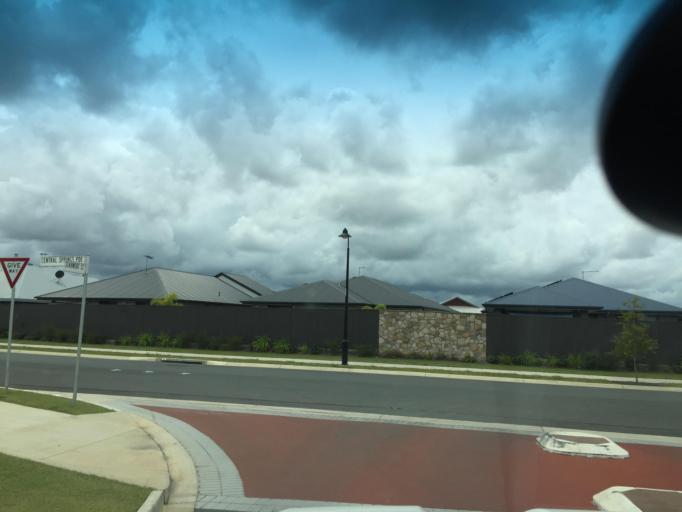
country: AU
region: Queensland
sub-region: Moreton Bay
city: Caboolture
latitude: -27.0631
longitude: 152.9255
